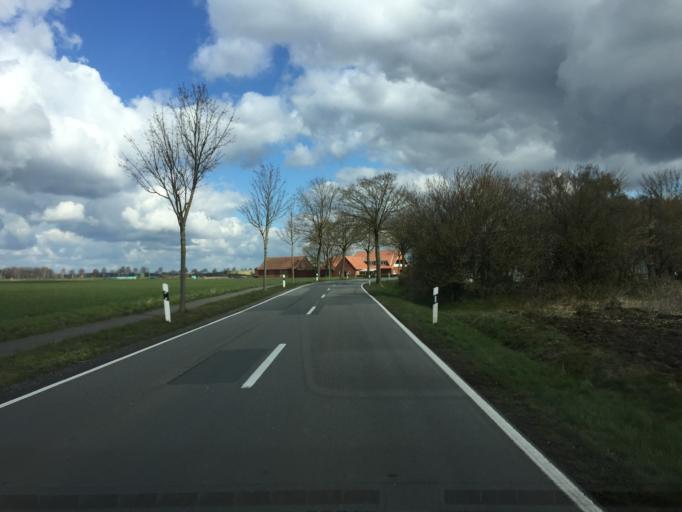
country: DE
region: Lower Saxony
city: Sudwalde
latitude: 52.7671
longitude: 8.8512
